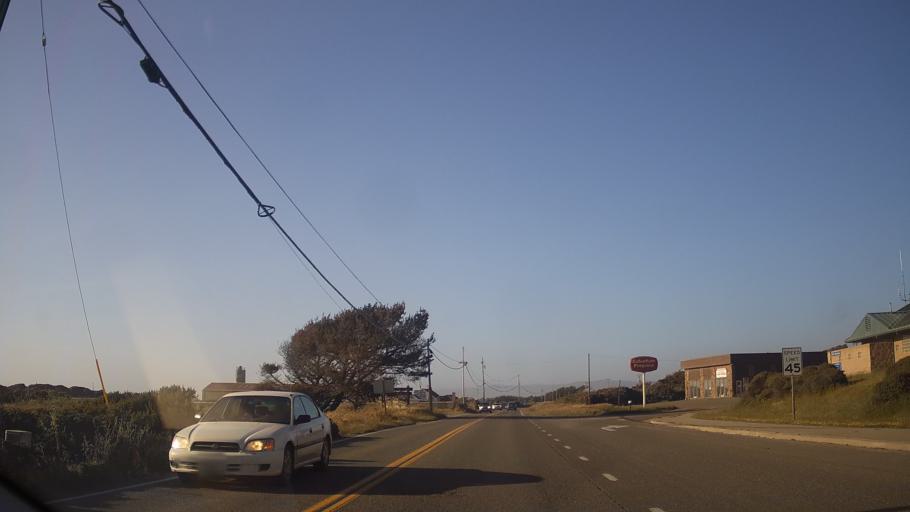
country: US
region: California
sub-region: Mendocino County
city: Fort Bragg
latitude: 39.4635
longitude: -123.8055
